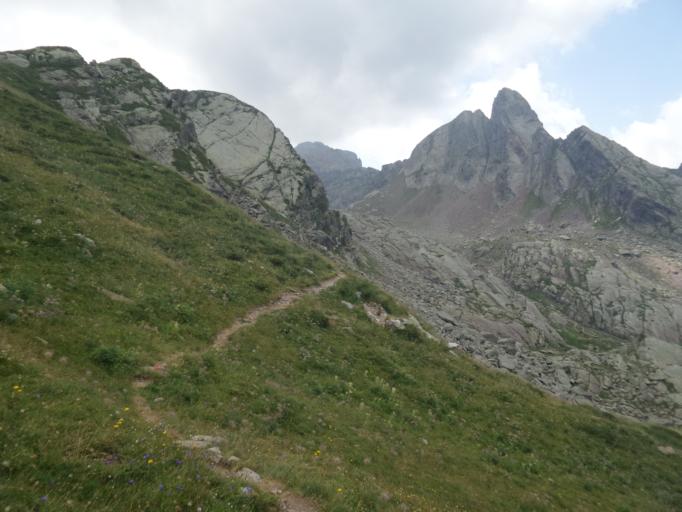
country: IT
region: Lombardy
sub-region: Provincia di Sondrio
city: Gerola Alta
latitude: 46.0305
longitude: 9.5221
